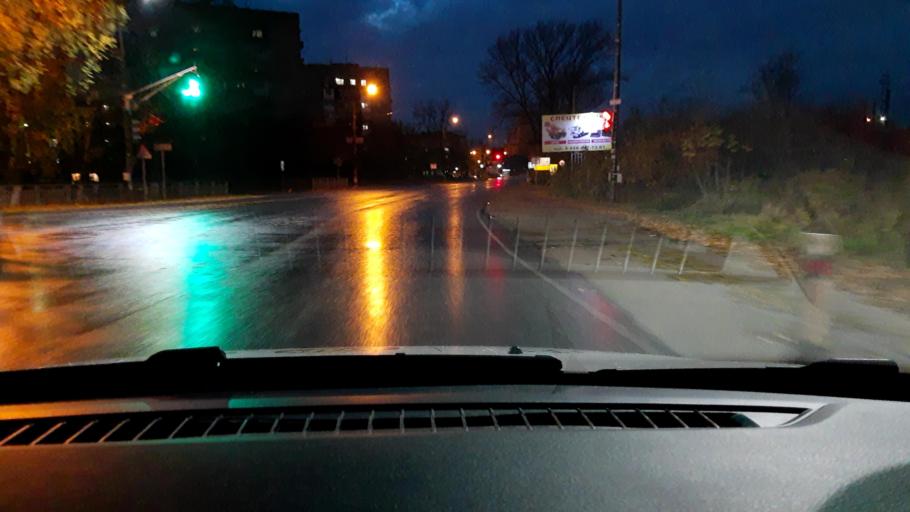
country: RU
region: Nizjnij Novgorod
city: Bor
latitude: 56.3536
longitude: 44.0754
